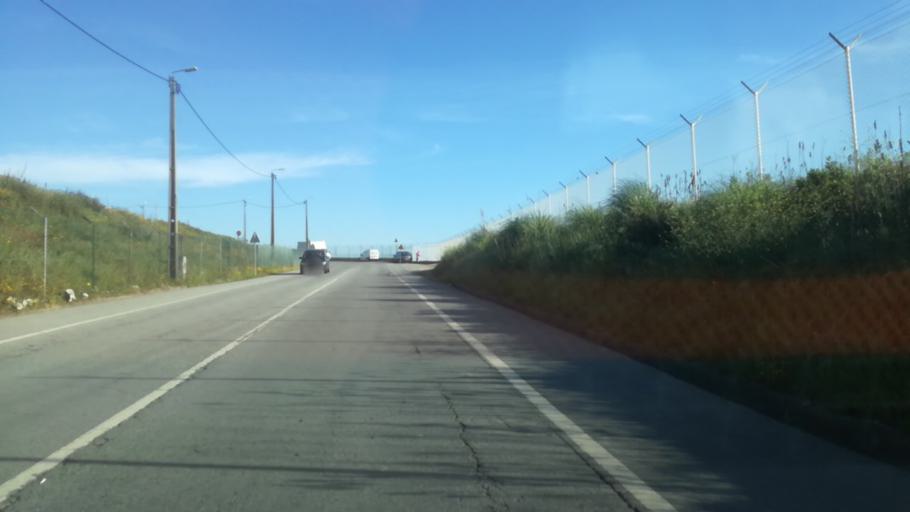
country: PT
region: Porto
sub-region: Matosinhos
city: Santa Cruz do Bispo
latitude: 41.2500
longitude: -8.6796
